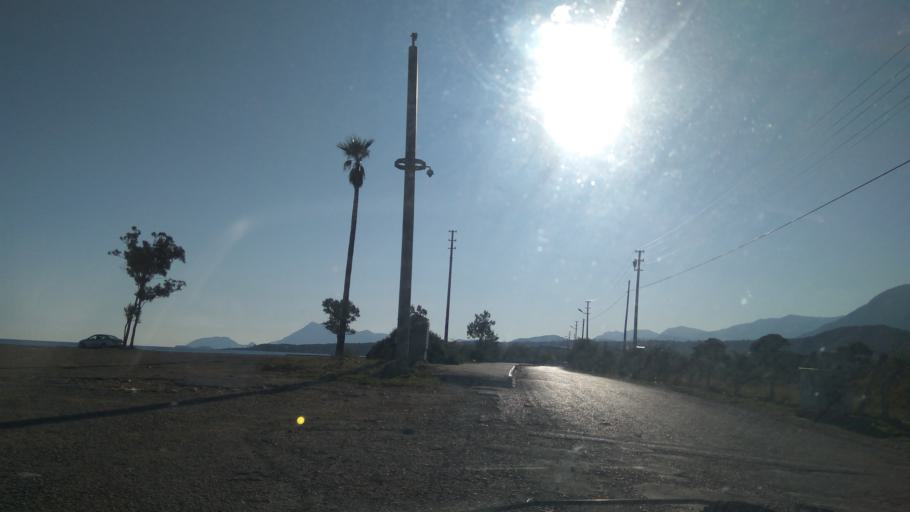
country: TR
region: Antalya
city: Kemer
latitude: 36.5608
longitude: 30.5724
